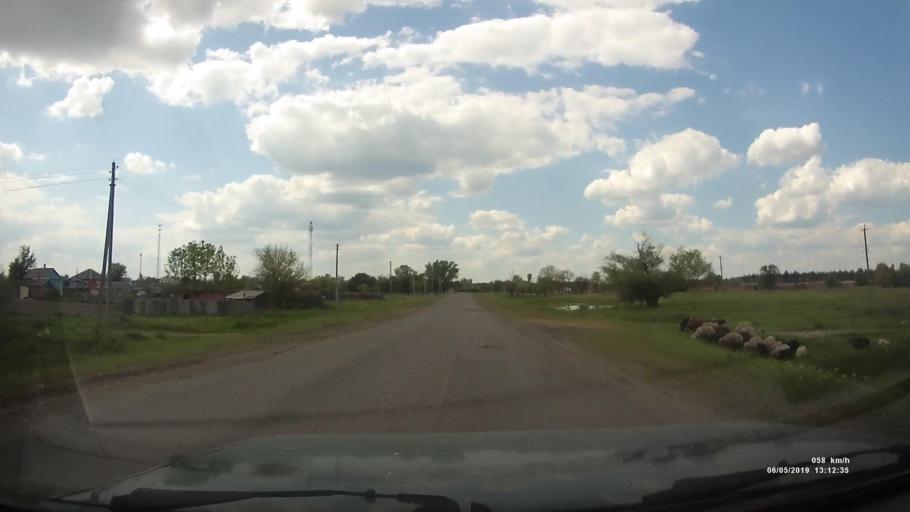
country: RU
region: Rostov
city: Ust'-Donetskiy
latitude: 47.7553
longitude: 40.9450
